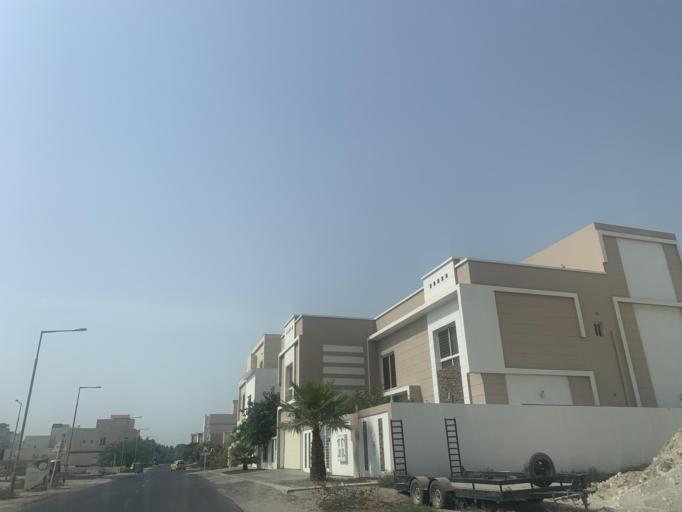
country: BH
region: Manama
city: Jidd Hafs
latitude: 26.2059
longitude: 50.4645
